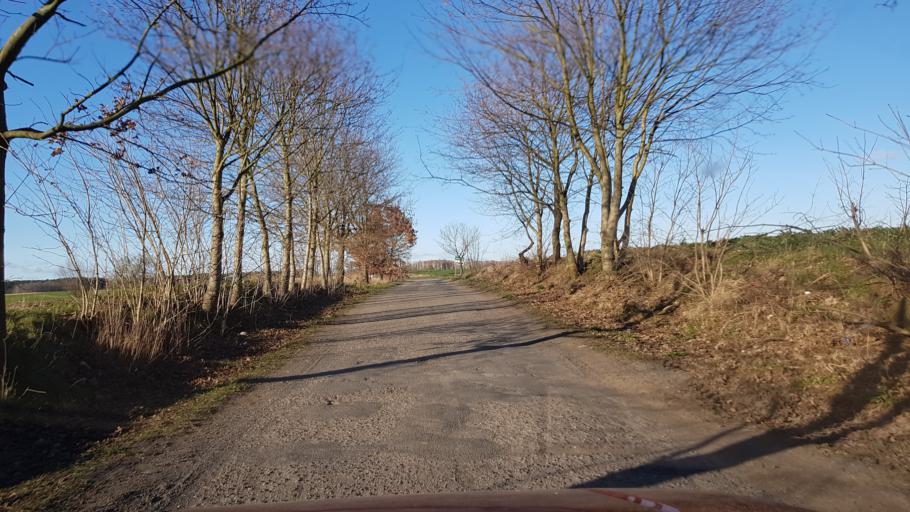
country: PL
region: West Pomeranian Voivodeship
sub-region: Powiat stargardzki
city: Stara Dabrowa
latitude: 53.3793
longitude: 15.1117
